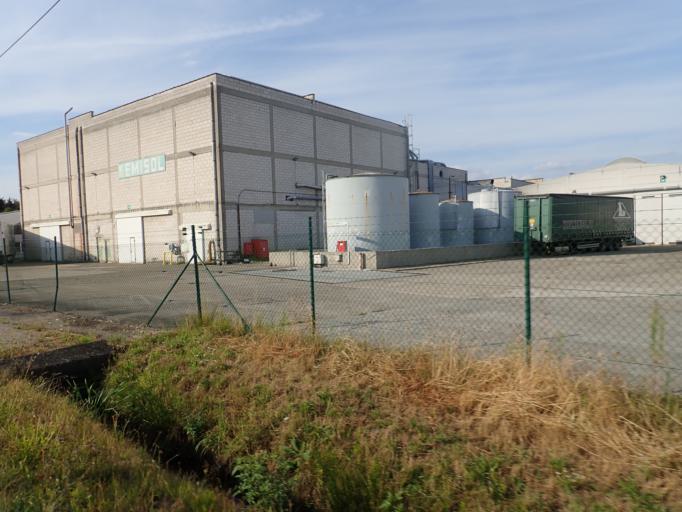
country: BE
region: Flanders
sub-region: Provincie Antwerpen
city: Hulshout
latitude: 51.0882
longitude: 4.7675
